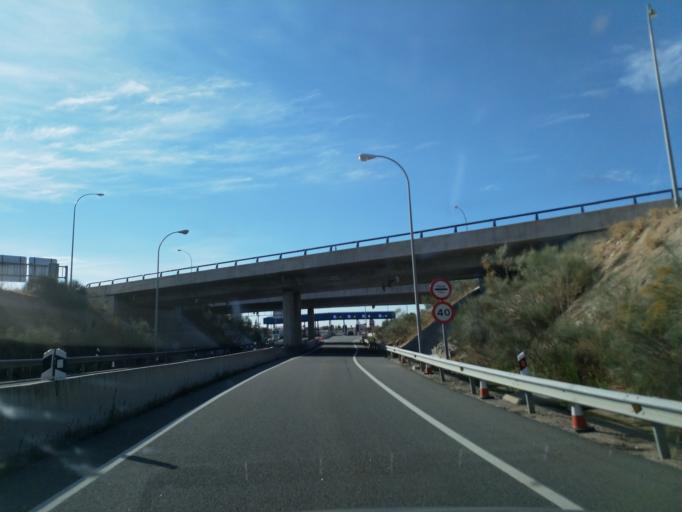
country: ES
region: Castille and Leon
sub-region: Provincia de Segovia
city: Villacastin
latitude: 40.7717
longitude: -4.4221
